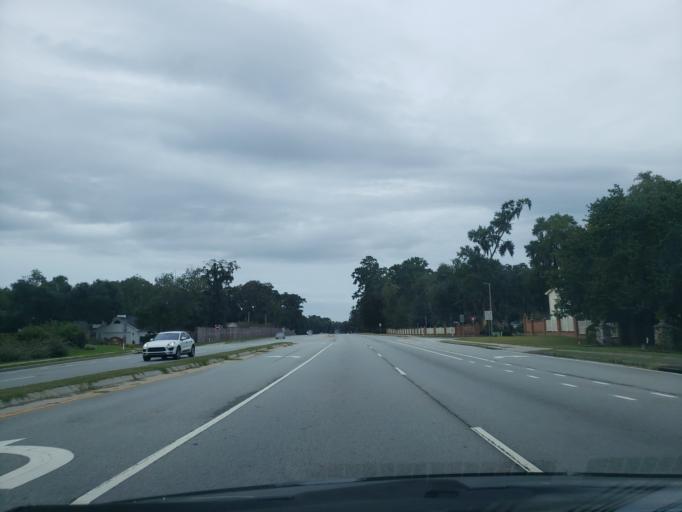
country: US
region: Georgia
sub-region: Chatham County
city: Montgomery
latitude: 31.9707
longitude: -81.1041
